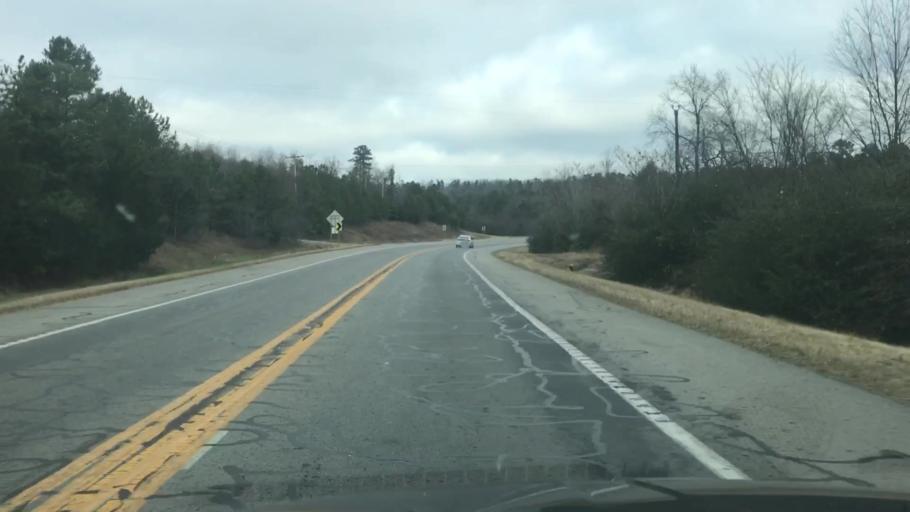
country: US
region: Arkansas
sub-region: Scott County
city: Waldron
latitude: 34.8102
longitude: -94.0398
